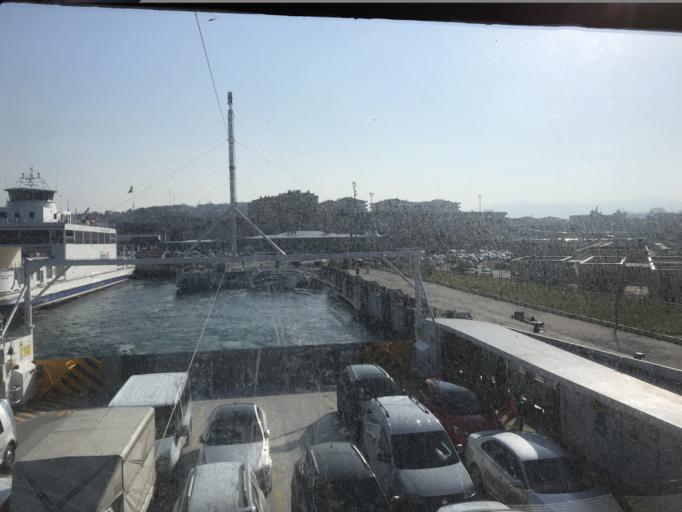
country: TR
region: Yalova
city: Yalova
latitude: 40.6617
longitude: 29.2792
